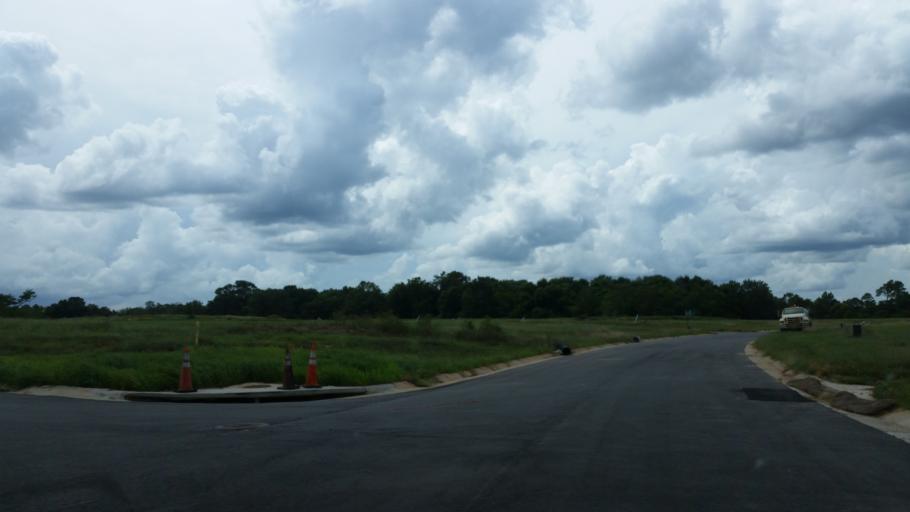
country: US
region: Florida
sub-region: Escambia County
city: Cantonment
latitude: 30.5385
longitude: -87.4088
